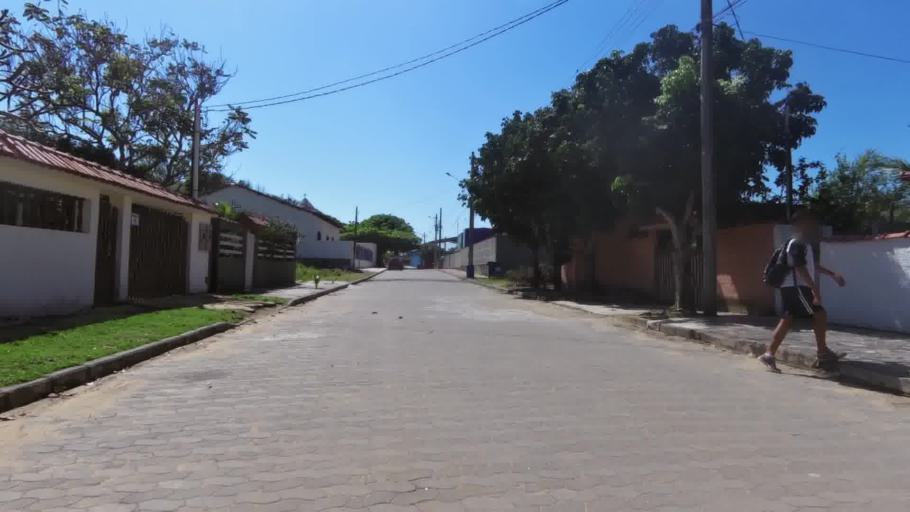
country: BR
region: Espirito Santo
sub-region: Piuma
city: Piuma
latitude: -20.8315
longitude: -40.6225
